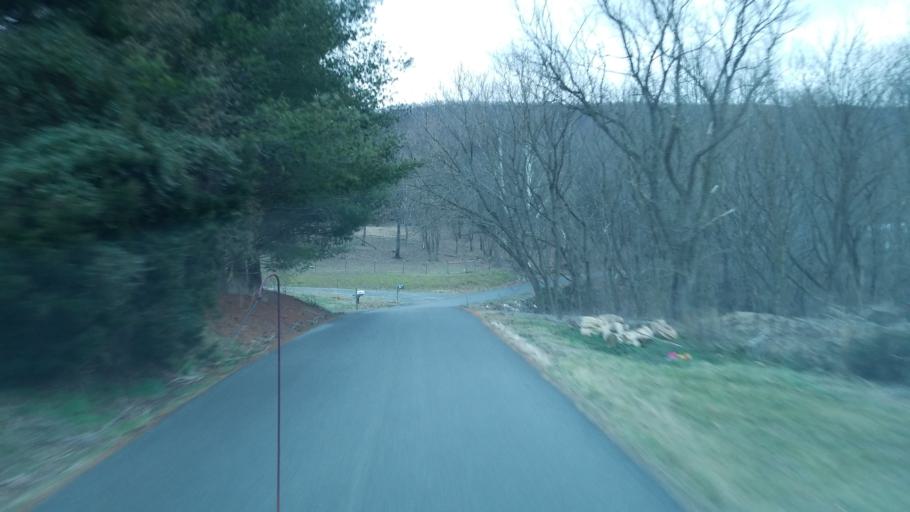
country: US
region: Virginia
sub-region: Pulaski County
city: Pulaski
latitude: 37.1588
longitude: -80.8666
